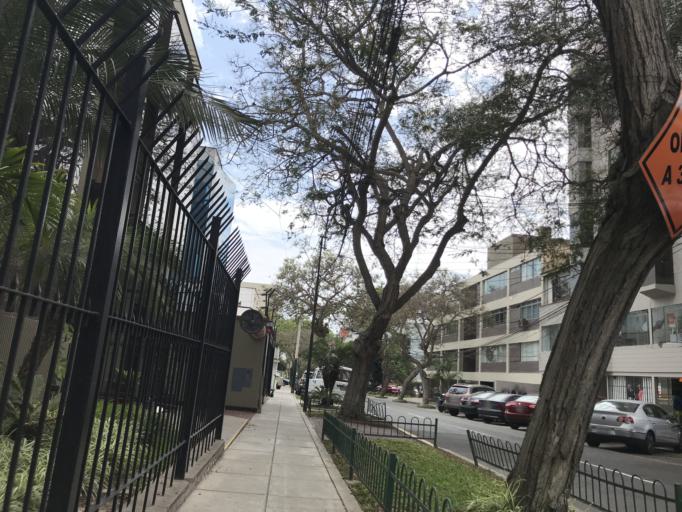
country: PE
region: Lima
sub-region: Lima
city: San Isidro
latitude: -12.1073
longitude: -77.0404
